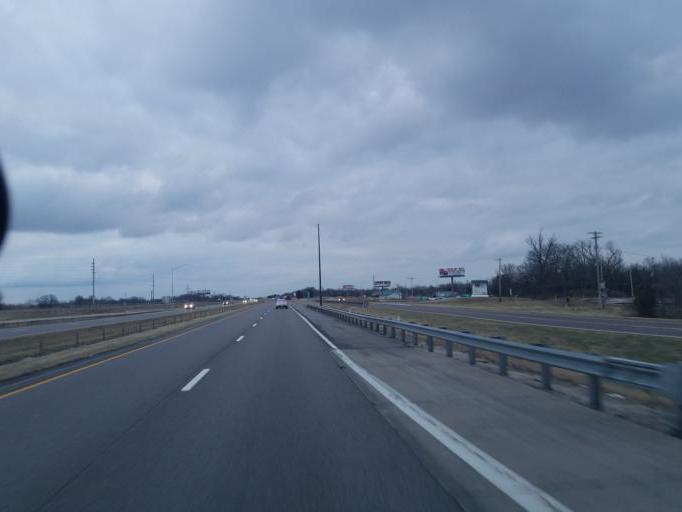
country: US
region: Missouri
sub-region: Saint Charles County
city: Wentzville
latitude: 38.8107
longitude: -90.9316
